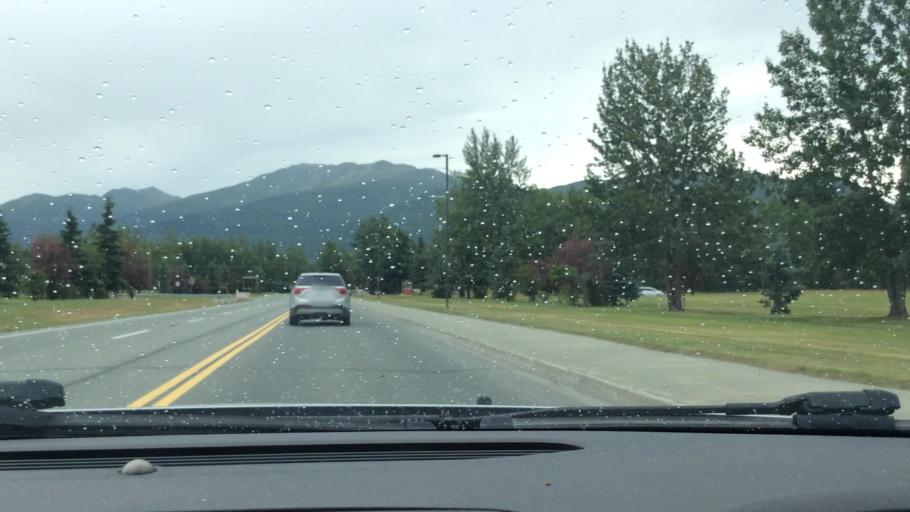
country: US
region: Alaska
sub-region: Anchorage Municipality
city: Elmendorf Air Force Base
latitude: 61.2587
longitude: -149.6724
